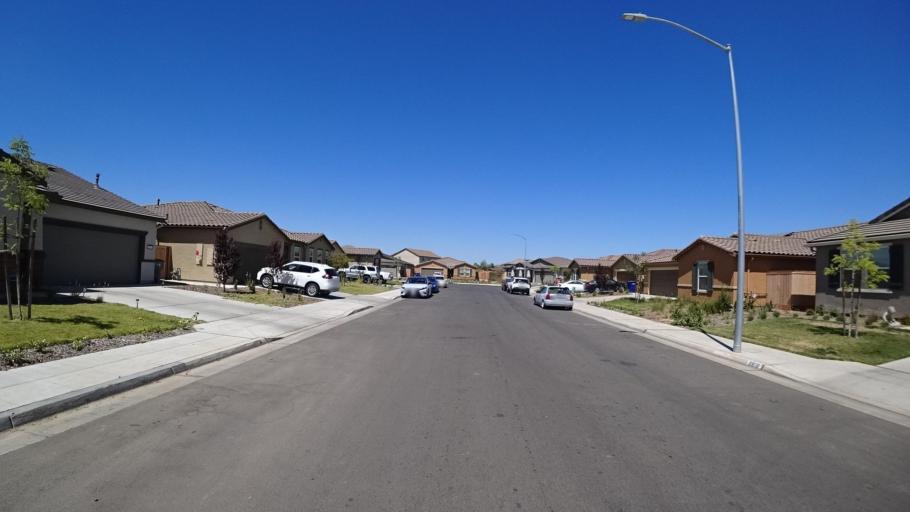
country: US
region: California
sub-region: Fresno County
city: Sunnyside
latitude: 36.7240
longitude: -119.6675
